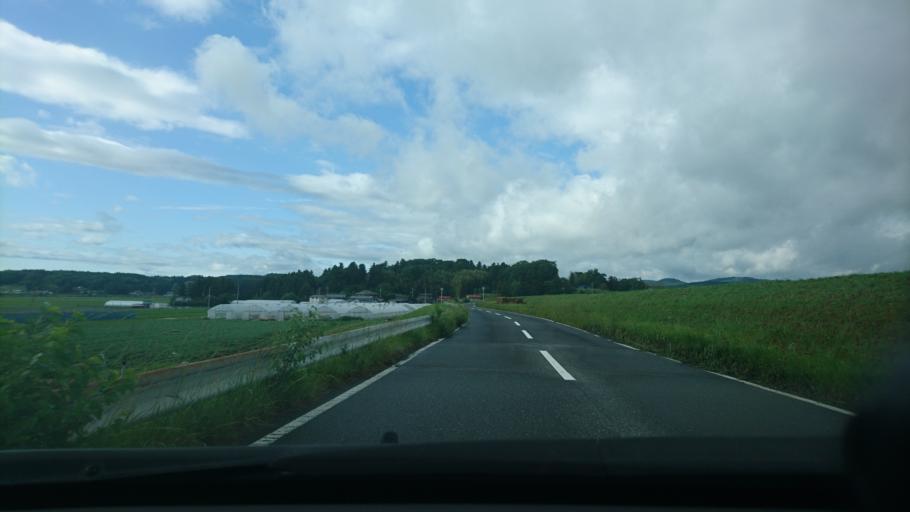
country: JP
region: Miyagi
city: Wakuya
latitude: 38.6864
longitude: 141.2836
